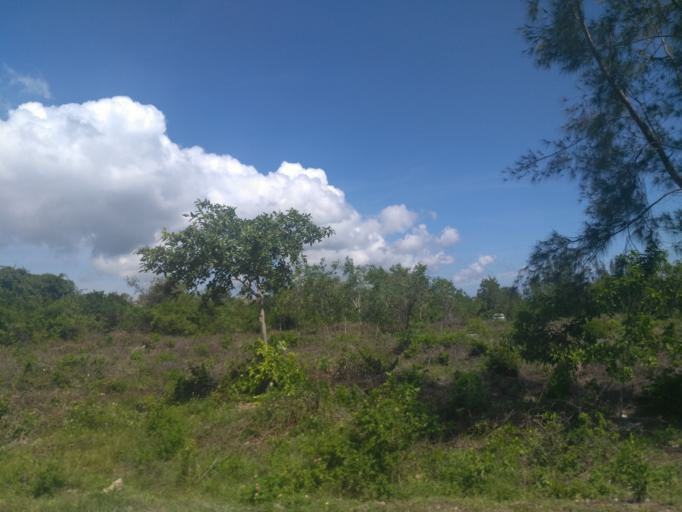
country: TZ
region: Zanzibar North
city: Gamba
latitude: -5.9255
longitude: 39.3523
